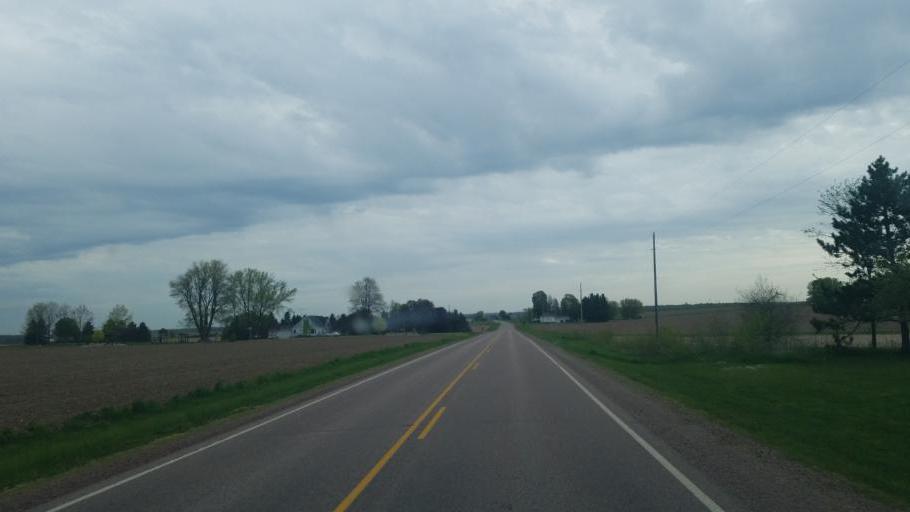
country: US
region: Wisconsin
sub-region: Wood County
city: Marshfield
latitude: 44.5932
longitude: -90.2988
